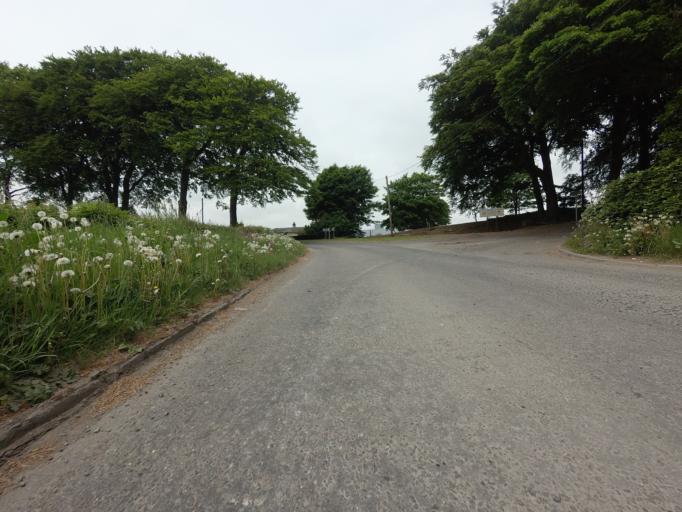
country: GB
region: Scotland
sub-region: Fife
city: Townhill
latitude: 56.0986
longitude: -3.4451
